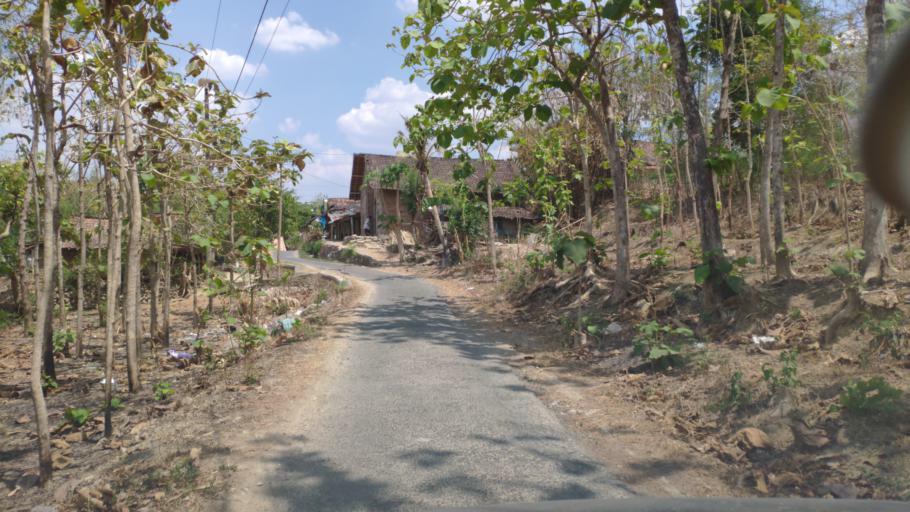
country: ID
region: Central Java
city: Prantaan
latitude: -6.9491
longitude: 111.5013
